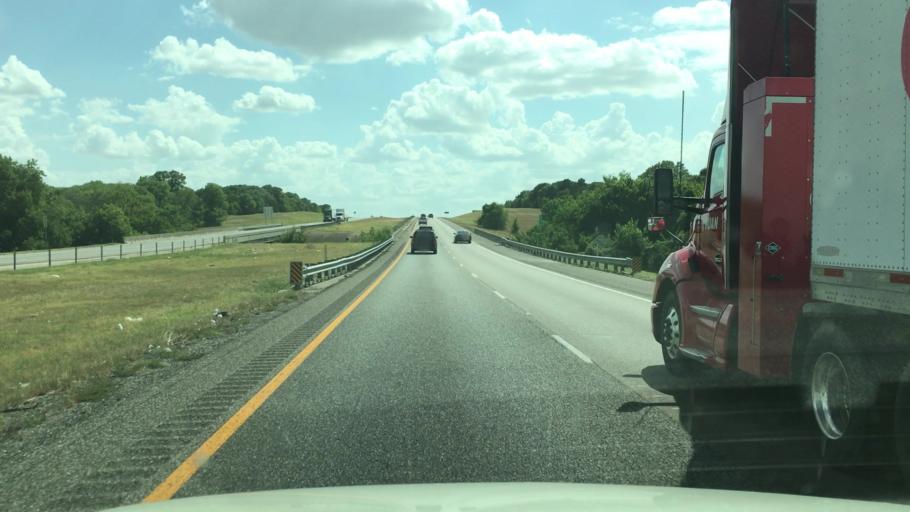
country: US
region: Texas
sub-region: Ellis County
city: Plum Grove
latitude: 32.0951
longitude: -97.0251
